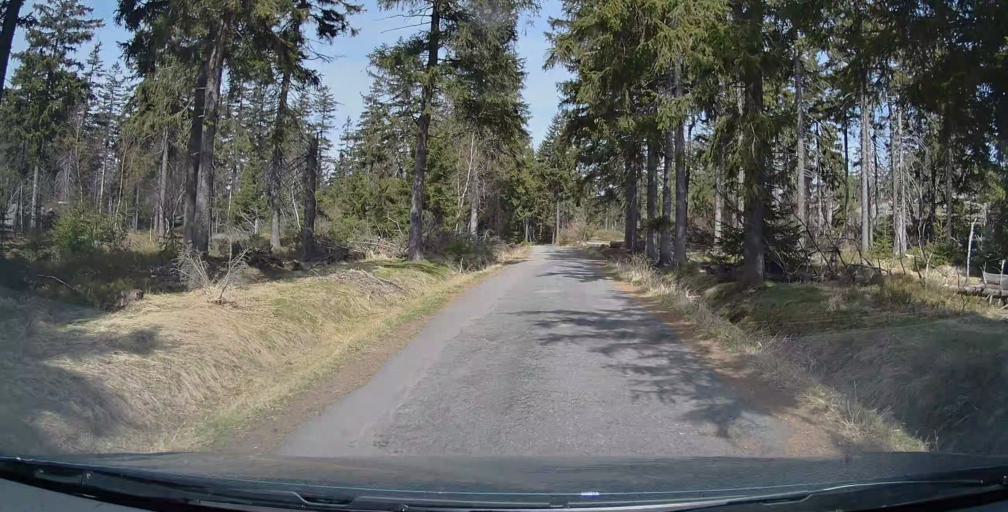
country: CZ
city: Machov
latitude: 50.4765
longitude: 16.2878
